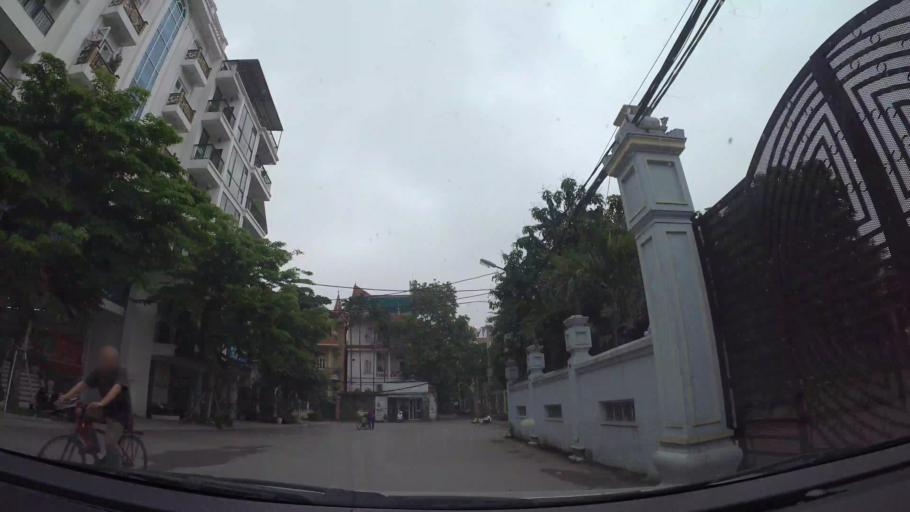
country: VN
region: Ha Noi
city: Tay Ho
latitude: 21.0671
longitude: 105.8228
